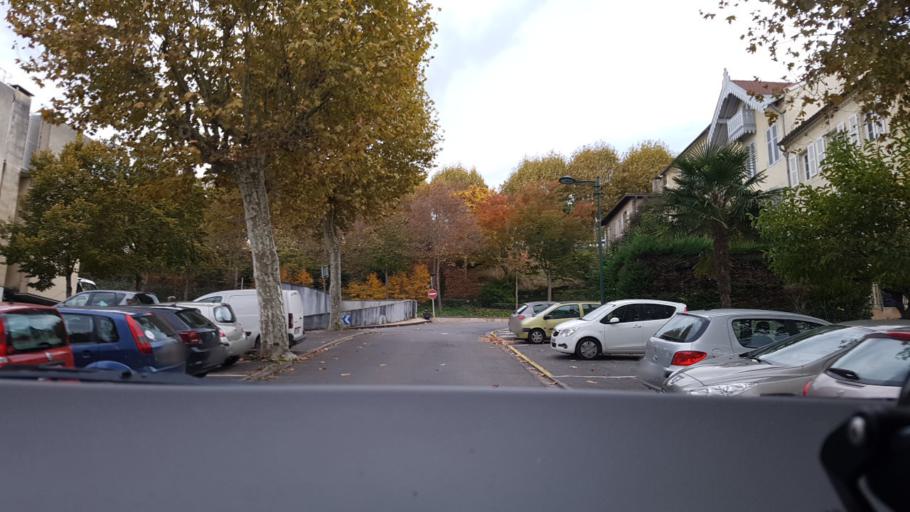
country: FR
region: Midi-Pyrenees
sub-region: Departement du Gers
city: Auch
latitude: 43.6491
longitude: 0.5827
